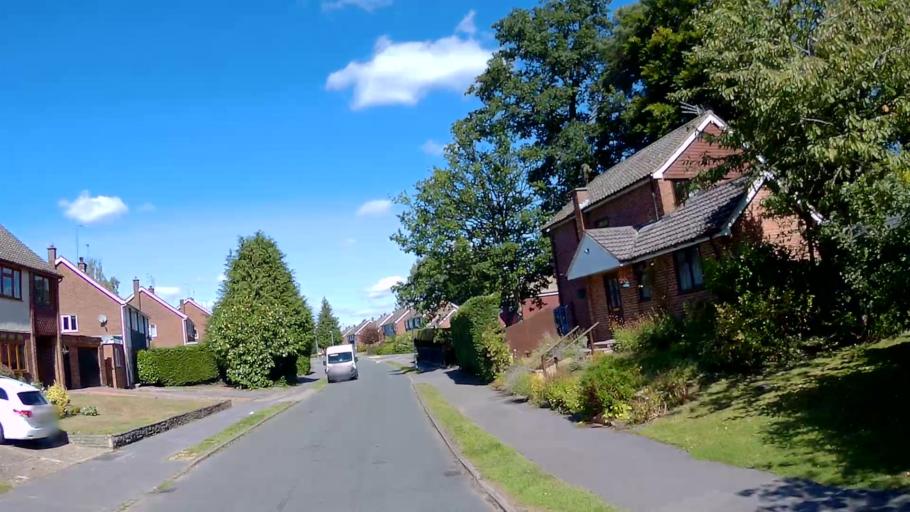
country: GB
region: England
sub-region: Bracknell Forest
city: Crowthorne
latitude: 51.3753
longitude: -0.8002
